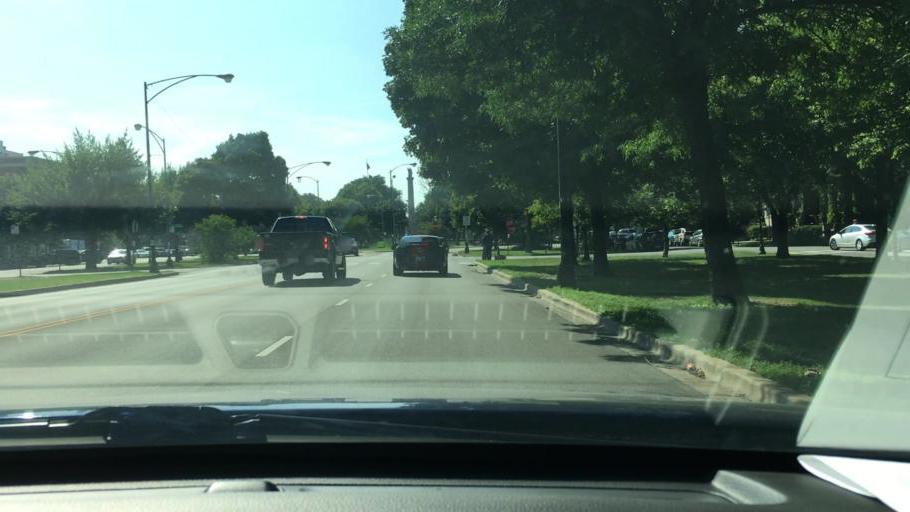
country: US
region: Illinois
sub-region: Cook County
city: Lincolnwood
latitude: 41.9286
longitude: -87.7042
